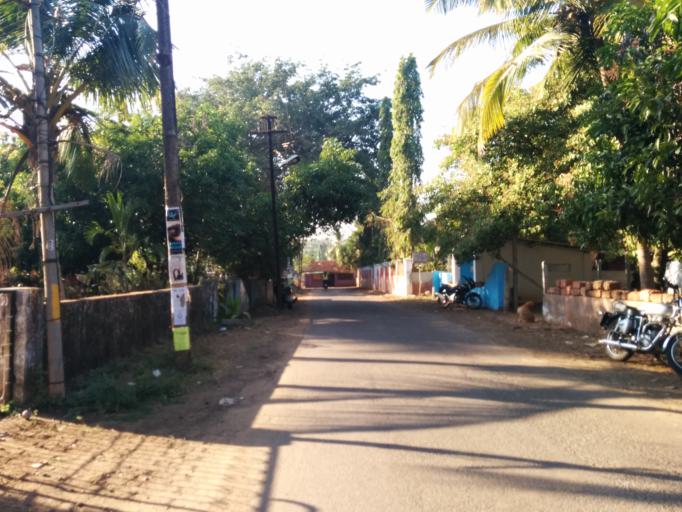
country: IN
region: Karnataka
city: Canacona
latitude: 14.9985
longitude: 74.0361
